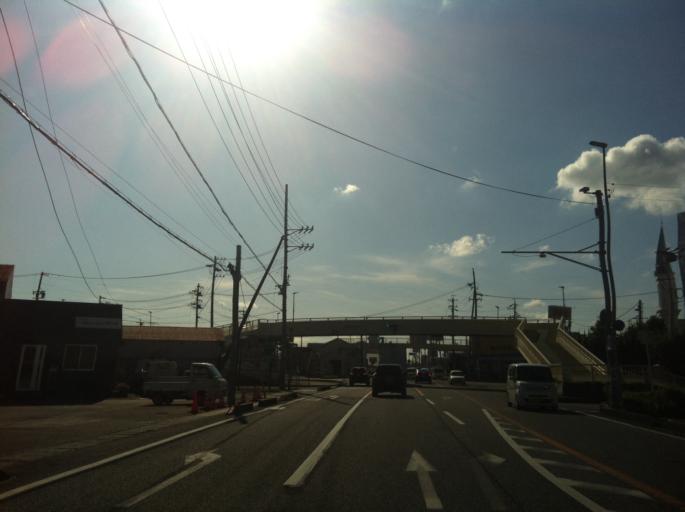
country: JP
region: Shizuoka
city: Fujieda
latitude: 34.8946
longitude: 138.2827
